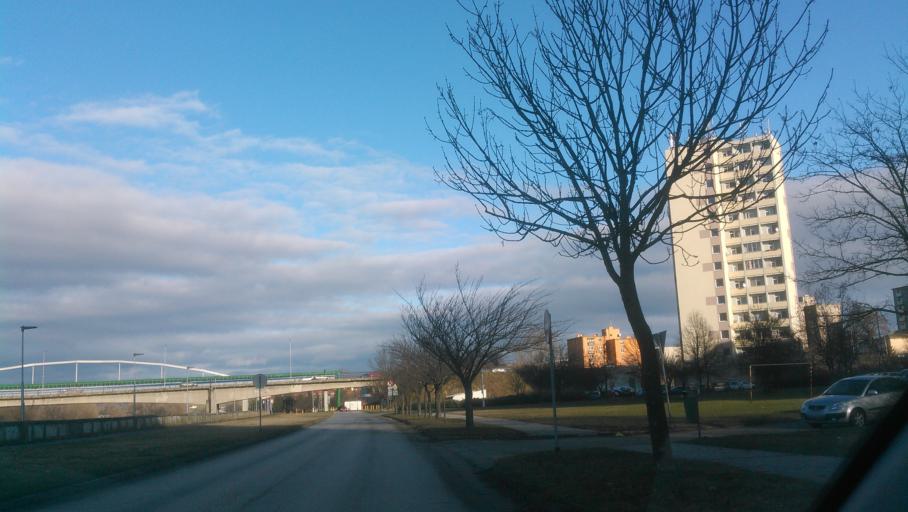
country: SK
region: Trnavsky
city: Hlohovec
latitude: 48.4277
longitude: 17.7913
